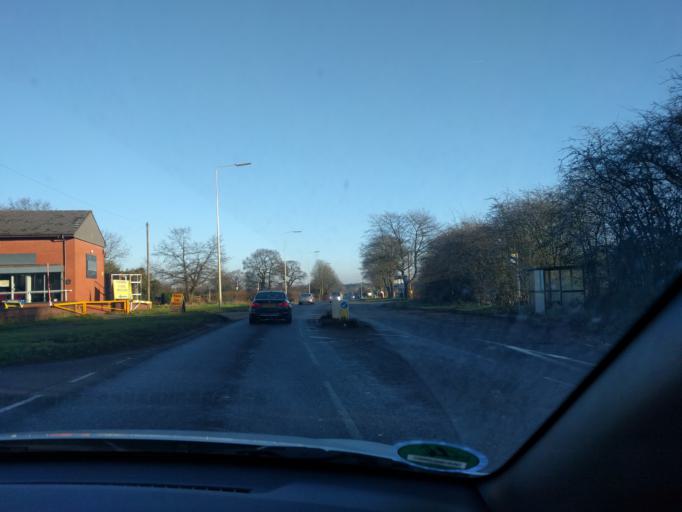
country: GB
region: England
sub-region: Staffordshire
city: Featherstone
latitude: 52.6529
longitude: -2.0788
